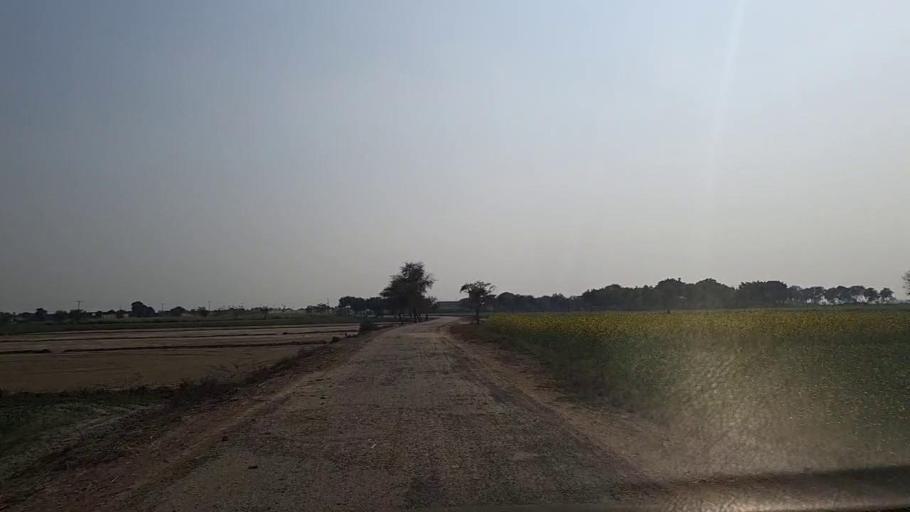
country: PK
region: Sindh
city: Daur
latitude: 26.4021
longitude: 68.4175
